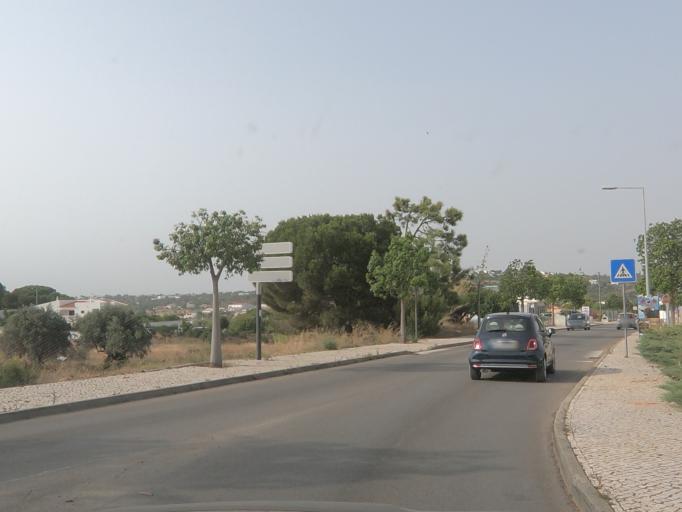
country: PT
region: Faro
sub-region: Albufeira
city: Guia
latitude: 37.0822
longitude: -8.2979
